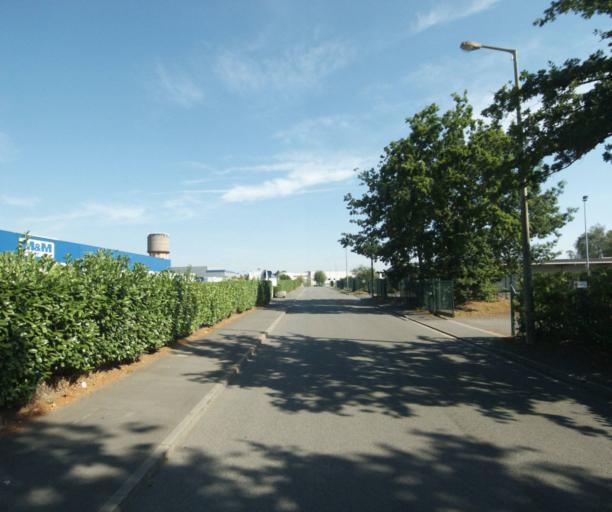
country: FR
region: Nord-Pas-de-Calais
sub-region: Departement du Nord
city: Halluin
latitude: 50.7864
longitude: 3.1421
